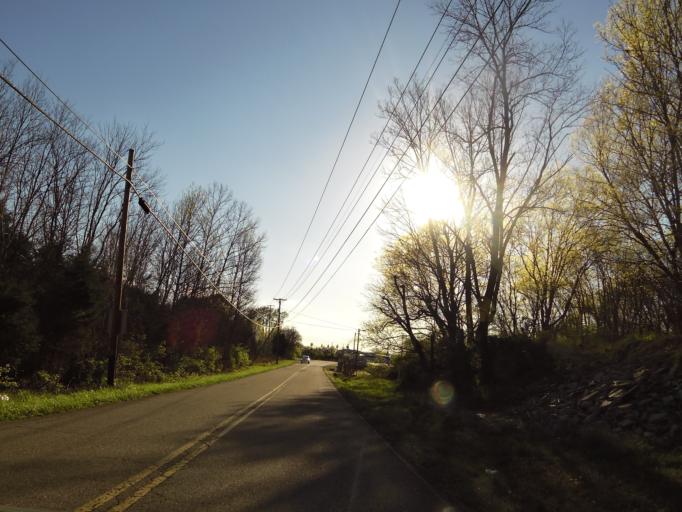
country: US
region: Tennessee
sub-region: Knox County
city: Knoxville
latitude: 35.9584
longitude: -83.8161
